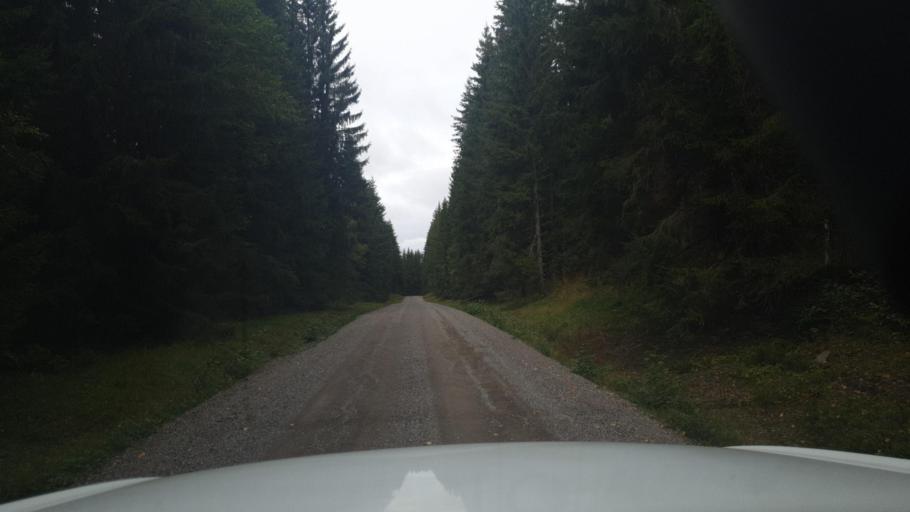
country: SE
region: Vaermland
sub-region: Eda Kommun
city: Charlottenberg
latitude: 60.0360
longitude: 12.6305
